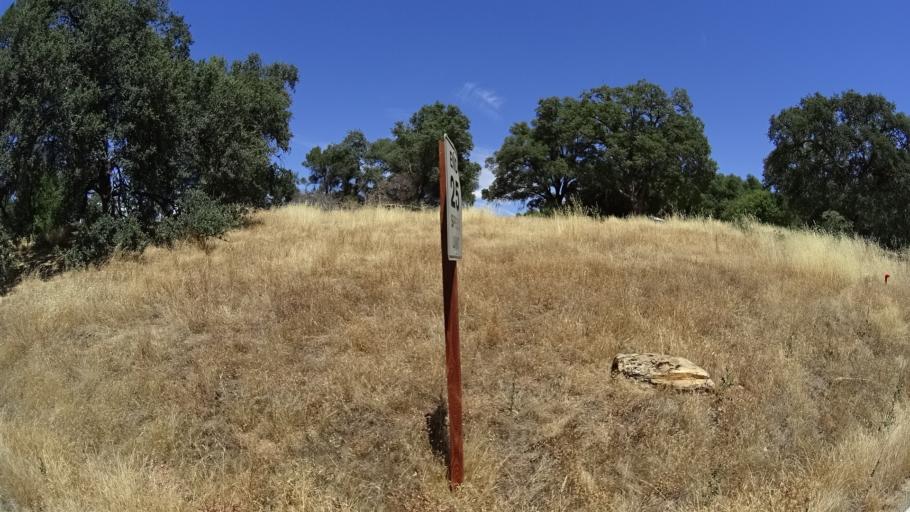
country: US
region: California
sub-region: Calaveras County
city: Forest Meadows
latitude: 38.2105
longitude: -120.4637
